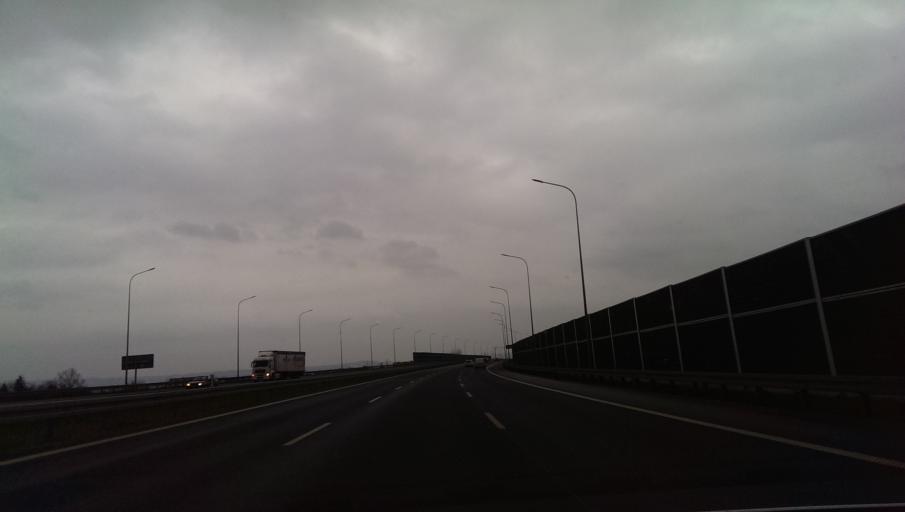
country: PL
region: Lesser Poland Voivodeship
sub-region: Powiat wielicki
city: Kokotow
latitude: 50.0439
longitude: 20.0691
